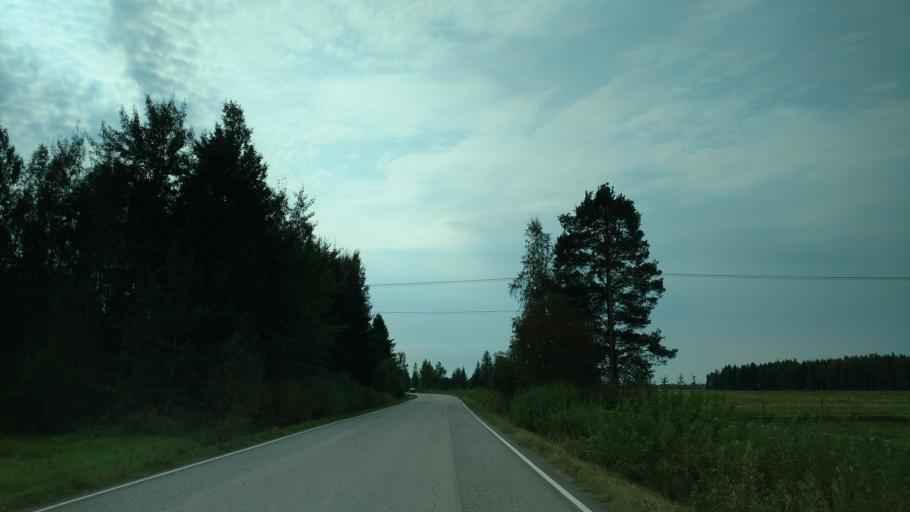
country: FI
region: Varsinais-Suomi
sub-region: Loimaa
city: Koski Tl
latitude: 60.6824
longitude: 23.1603
